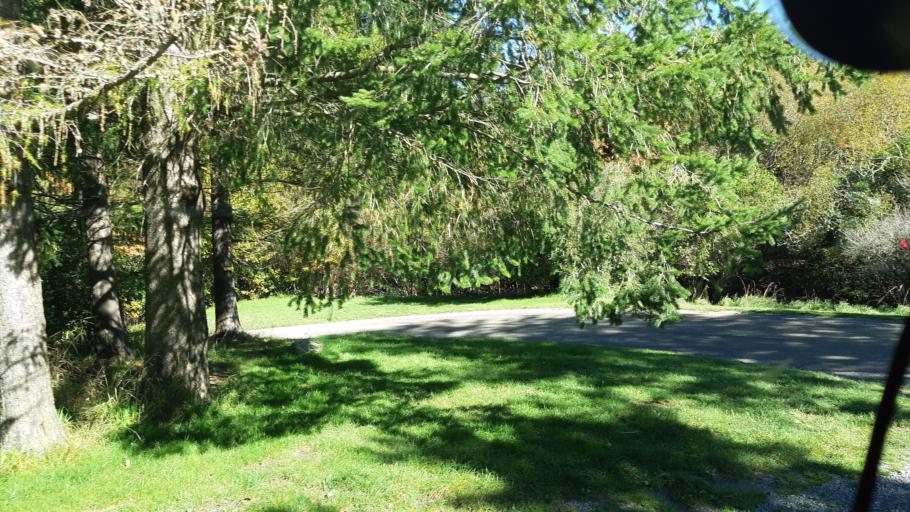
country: NZ
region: Canterbury
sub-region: Waimakariri District
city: Oxford
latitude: -43.1924
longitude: 172.3361
